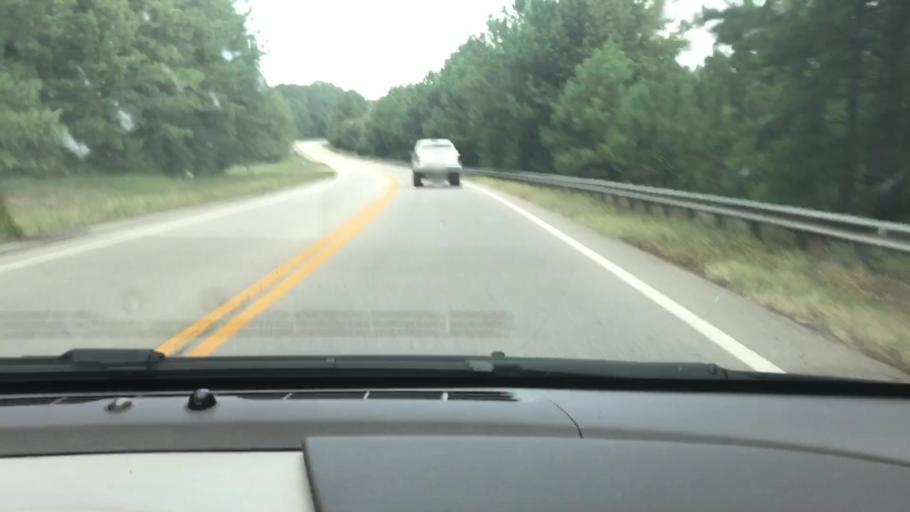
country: US
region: Georgia
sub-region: Troup County
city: La Grange
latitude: 32.9707
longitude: -85.0244
